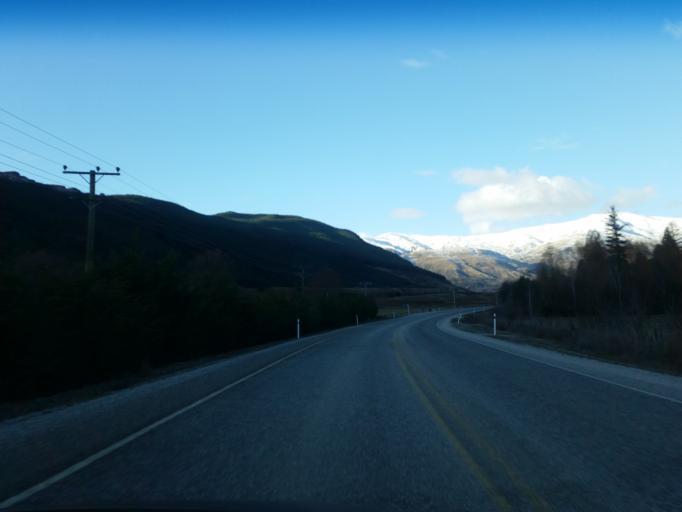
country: NZ
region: Otago
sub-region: Queenstown-Lakes District
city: Arrowtown
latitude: -44.9466
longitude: 168.7681
